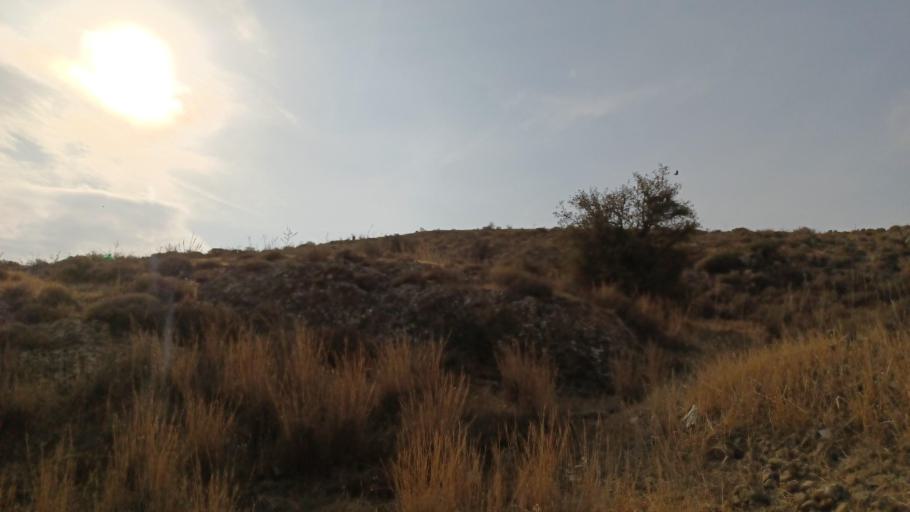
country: CY
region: Larnaka
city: Troulloi
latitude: 35.0242
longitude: 33.6105
